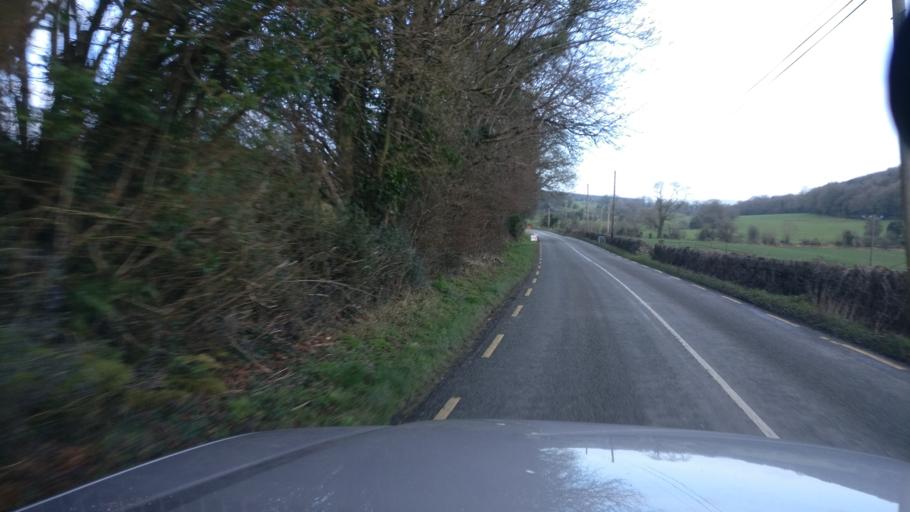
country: IE
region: Leinster
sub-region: Kilkenny
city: Castlecomer
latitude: 52.8168
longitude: -7.2135
